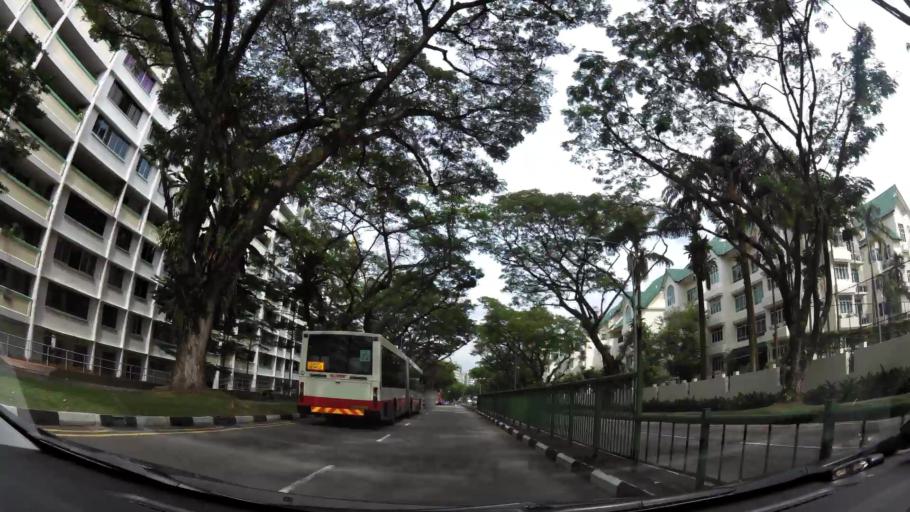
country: MY
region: Johor
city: Johor Bahru
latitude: 1.4300
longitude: 103.7817
